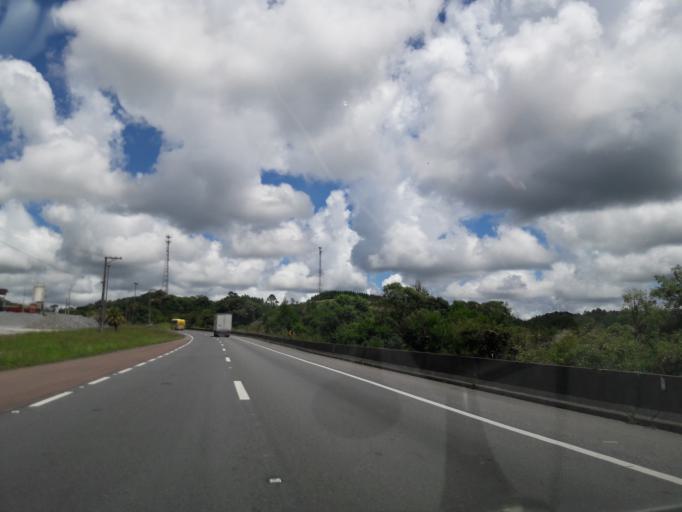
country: BR
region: Parana
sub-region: Campina Grande Do Sul
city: Campina Grande do Sul
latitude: -25.2978
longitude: -48.9400
